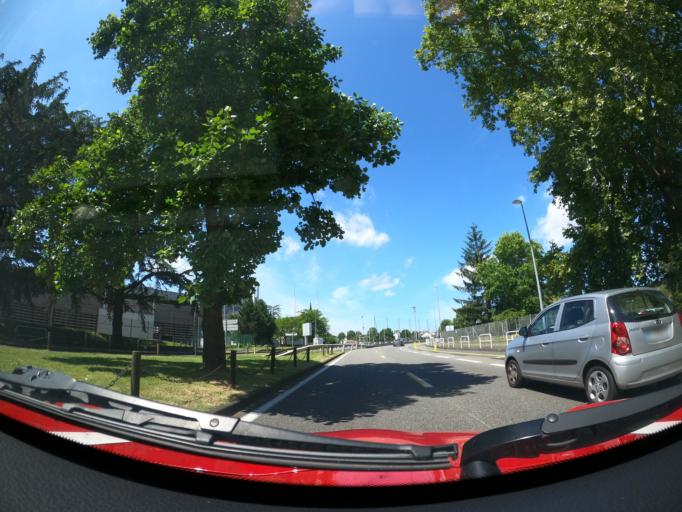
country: FR
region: Aquitaine
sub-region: Departement des Pyrenees-Atlantiques
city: Bayonne
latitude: 43.4866
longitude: -1.4787
